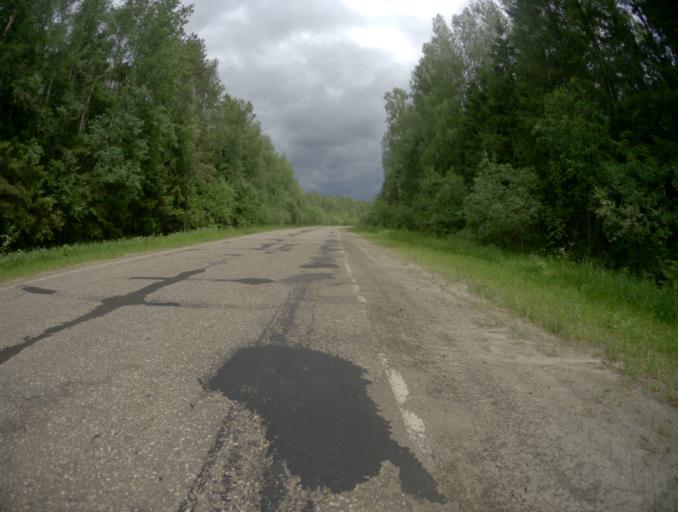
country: RU
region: Ivanovo
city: Arkhipovka
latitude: 56.6203
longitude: 41.2795
